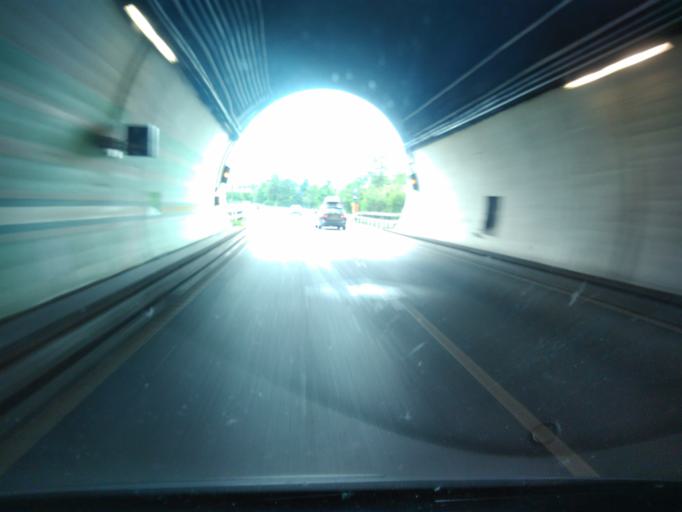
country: CH
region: Basel-Landschaft
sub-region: Bezirk Sissach
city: Itingen
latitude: 47.4768
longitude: 7.7794
